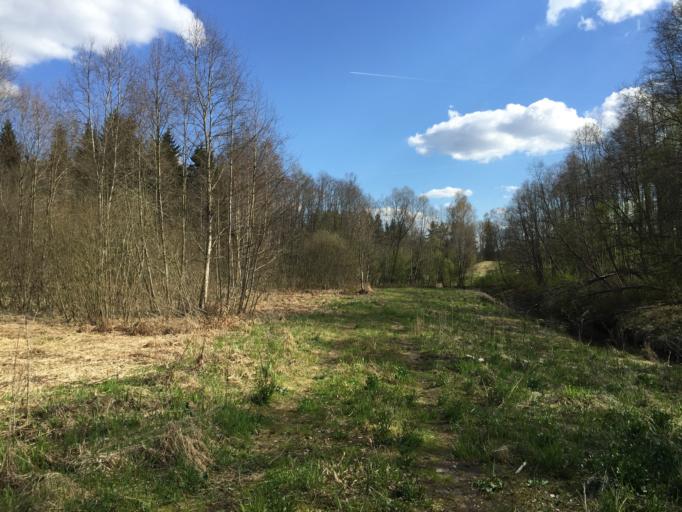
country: LV
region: Krimulda
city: Ragana
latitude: 57.3413
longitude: 24.6989
